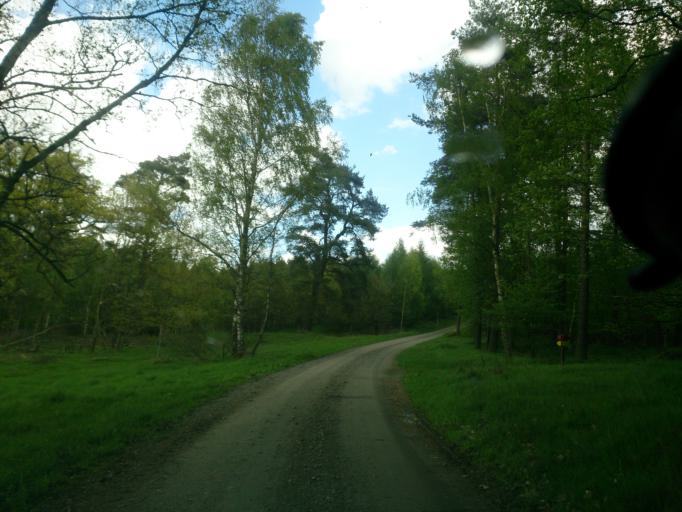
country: SE
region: Skane
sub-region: Sjobo Kommun
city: Sjoebo
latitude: 55.5608
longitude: 13.6998
